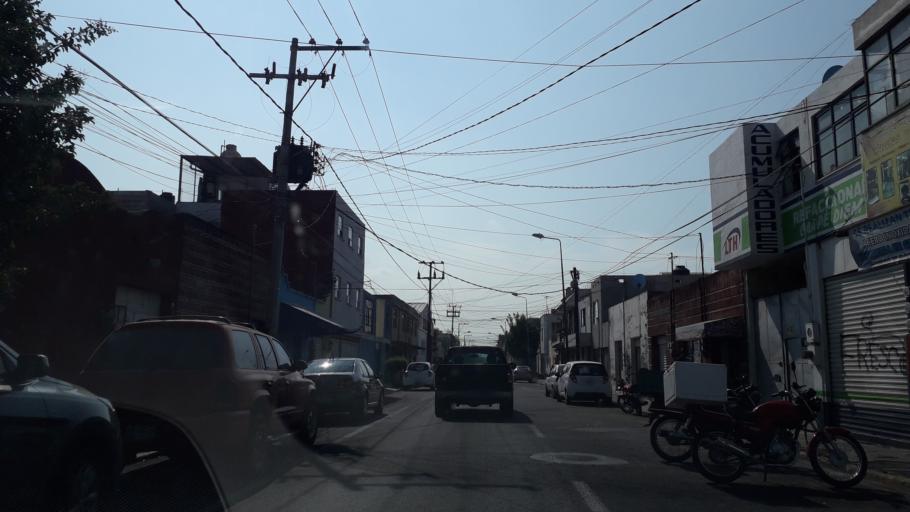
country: MX
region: Puebla
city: Puebla
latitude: 19.0432
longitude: -98.2156
